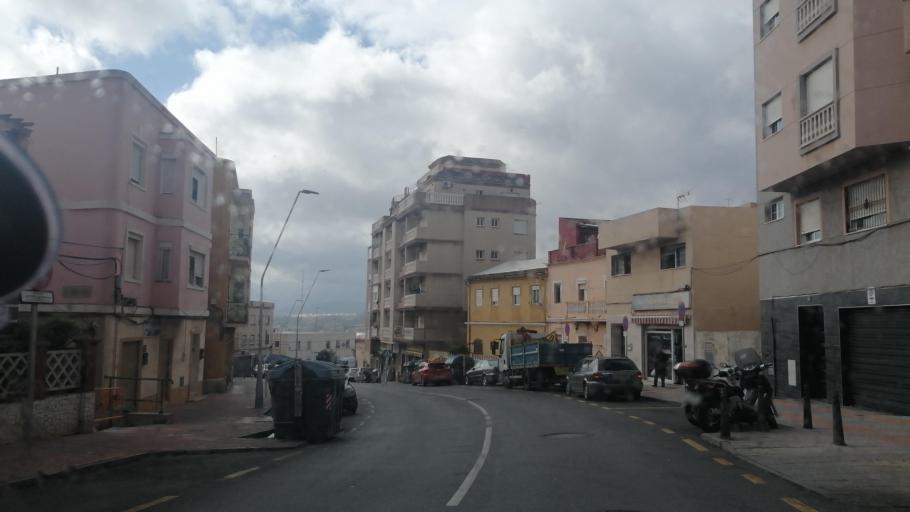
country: ES
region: Ceuta
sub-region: Ceuta
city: Ceuta
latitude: 35.8821
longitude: -5.3303
